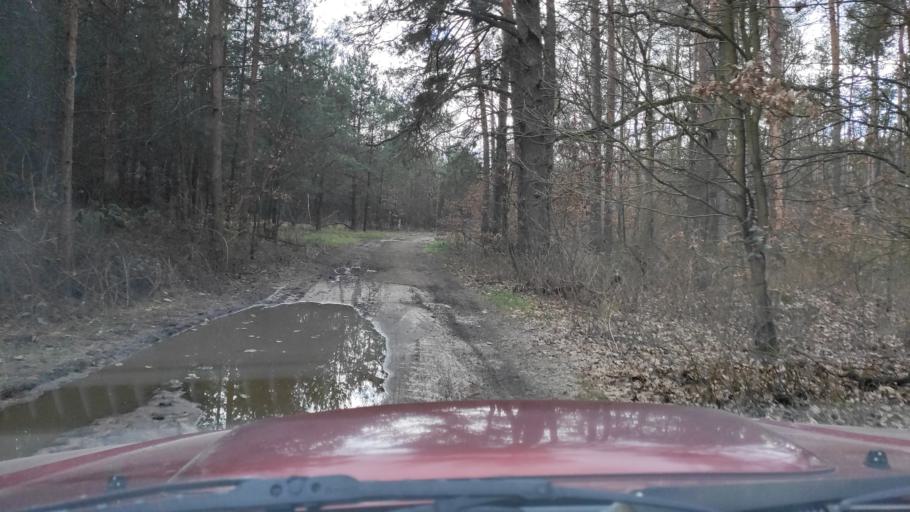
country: PL
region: Masovian Voivodeship
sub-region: Powiat kozienicki
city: Garbatka-Letnisko
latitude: 51.5129
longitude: 21.5641
